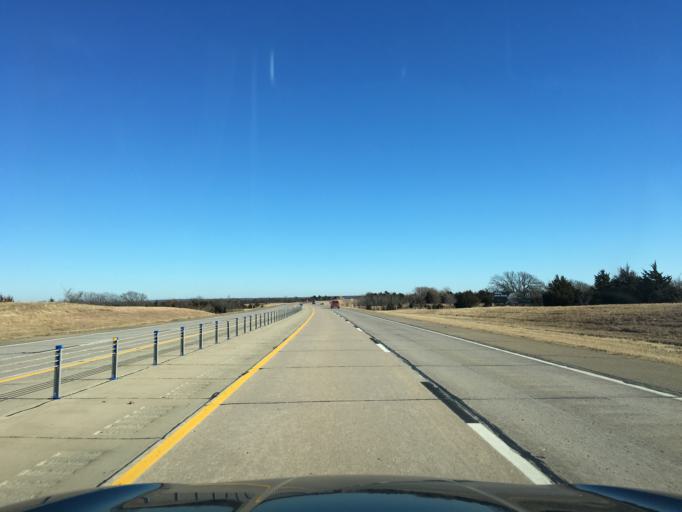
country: US
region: Oklahoma
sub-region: Pawnee County
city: Pawnee
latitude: 36.2249
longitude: -96.8876
